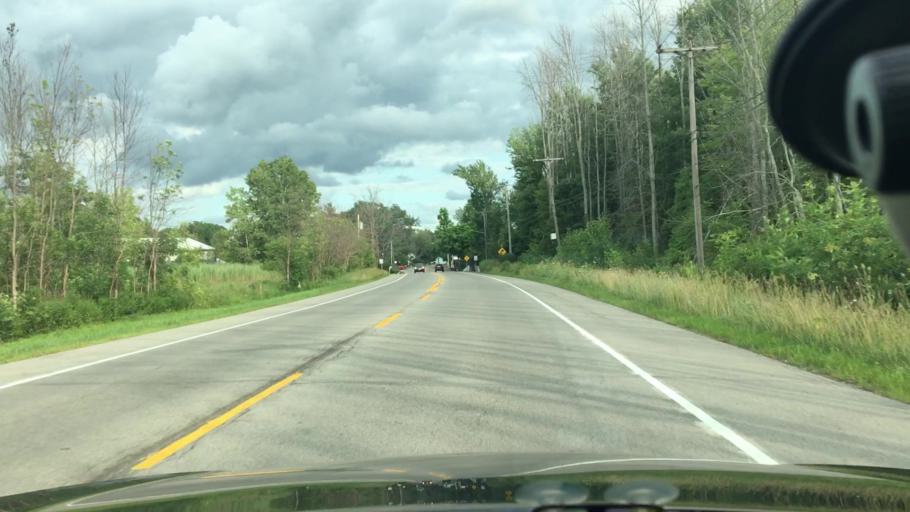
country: US
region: New York
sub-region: Erie County
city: Elma Center
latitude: 42.8237
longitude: -78.6856
